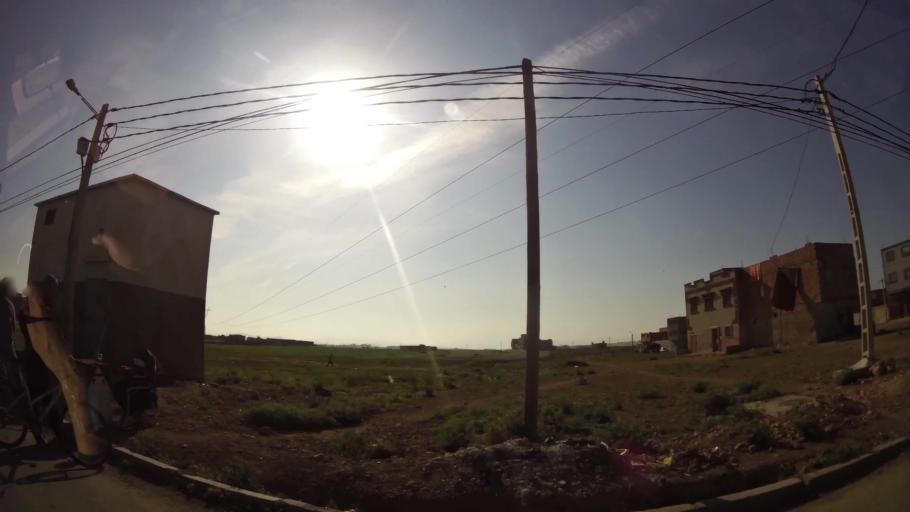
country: MA
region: Oriental
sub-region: Oujda-Angad
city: Oujda
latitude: 34.7218
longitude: -1.8920
